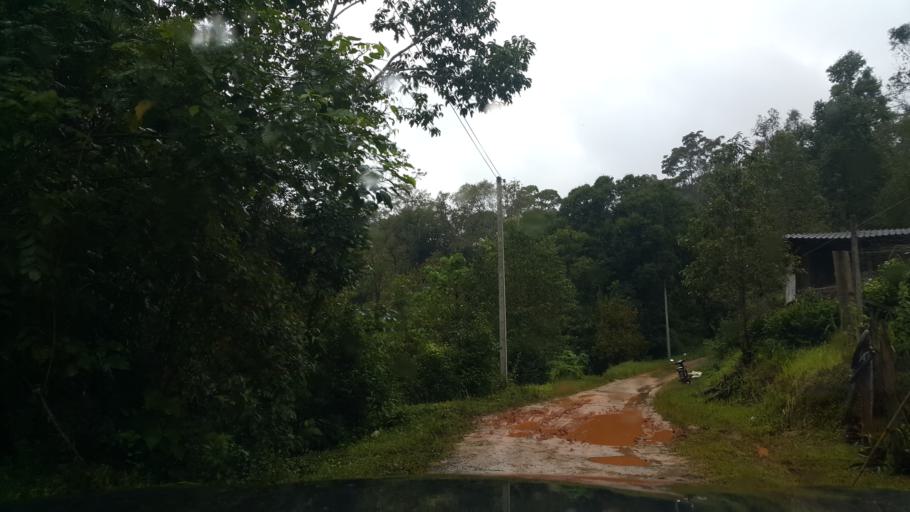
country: TH
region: Chiang Mai
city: Phrao
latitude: 19.1285
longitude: 99.3273
